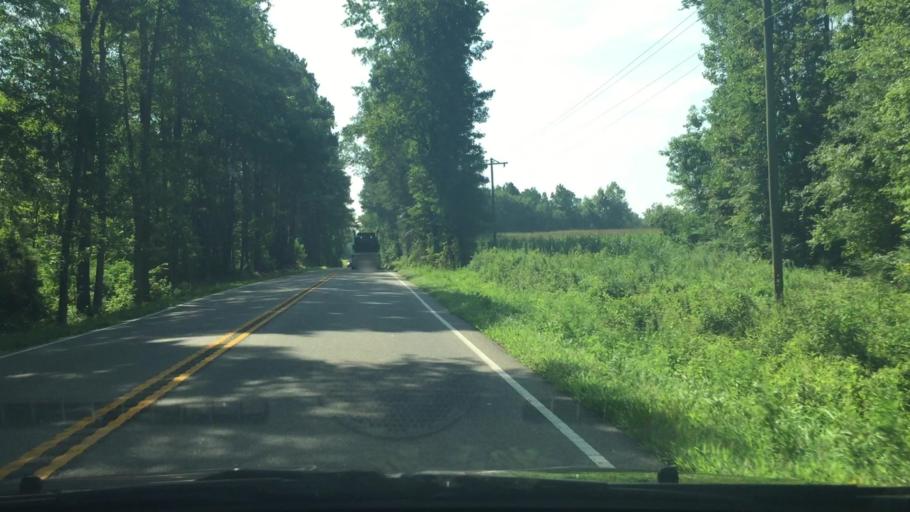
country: US
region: Virginia
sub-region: Sussex County
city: Sussex
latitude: 37.0214
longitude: -77.2873
